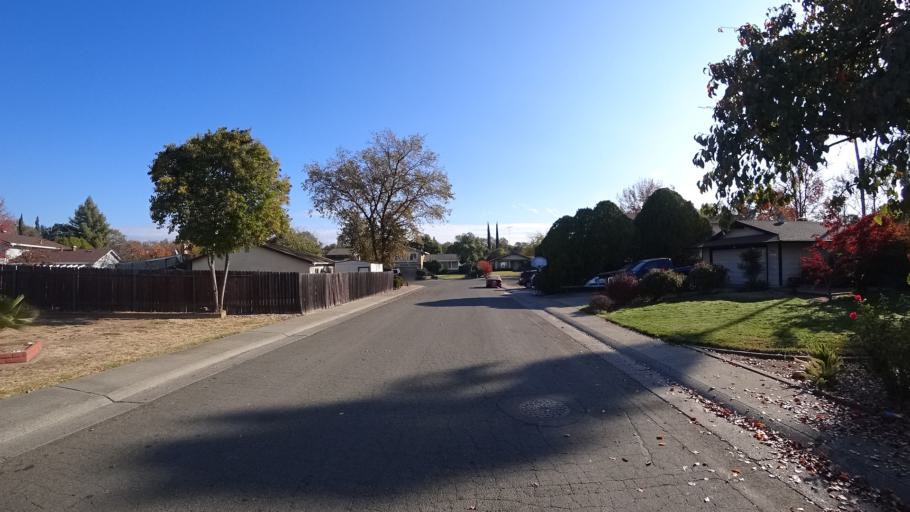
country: US
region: California
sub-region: Sacramento County
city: Citrus Heights
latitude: 38.7166
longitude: -121.2550
